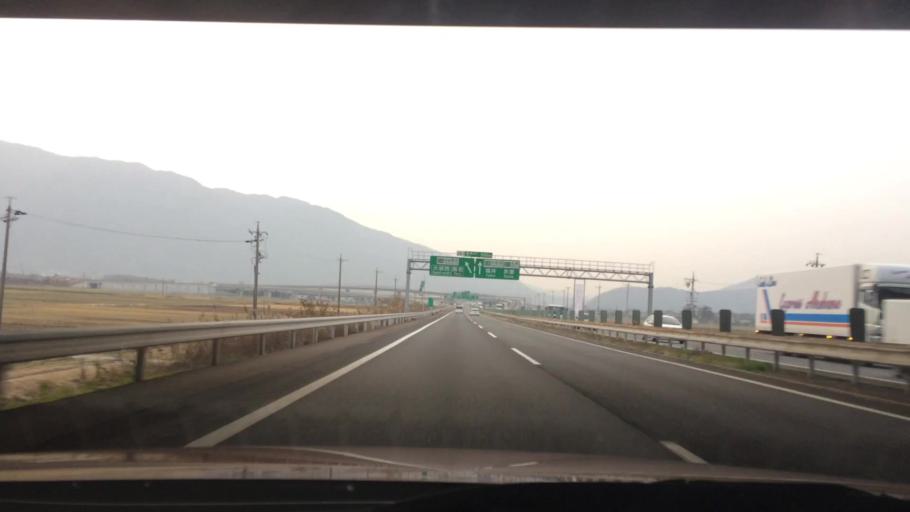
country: JP
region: Gifu
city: Ogaki
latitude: 35.3184
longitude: 136.5804
